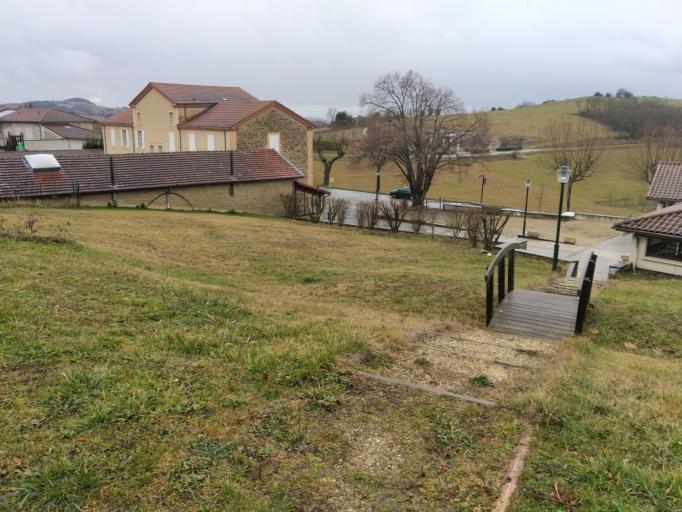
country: FR
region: Rhone-Alpes
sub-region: Departement de la Drome
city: Chateauneuf-de-Galaure
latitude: 45.2187
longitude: 4.9844
